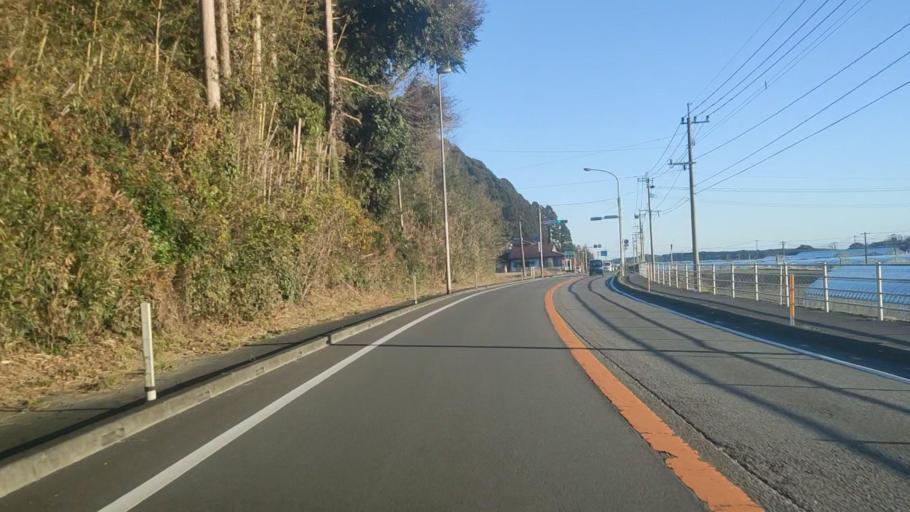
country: JP
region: Miyazaki
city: Takanabe
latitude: 32.0881
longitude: 131.5126
